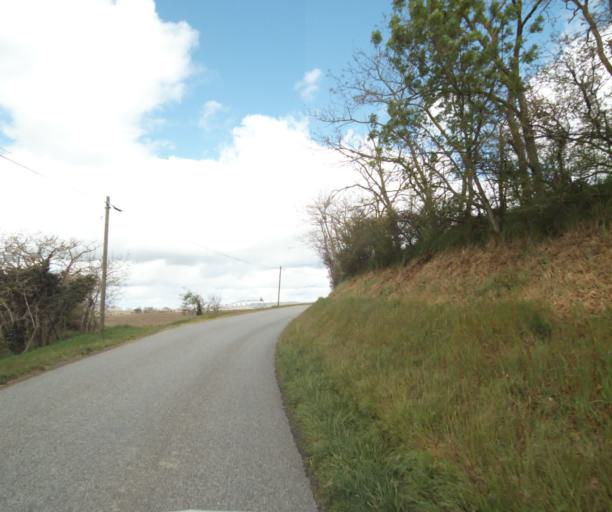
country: FR
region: Midi-Pyrenees
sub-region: Departement de l'Ariege
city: Saverdun
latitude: 43.2467
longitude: 1.5897
